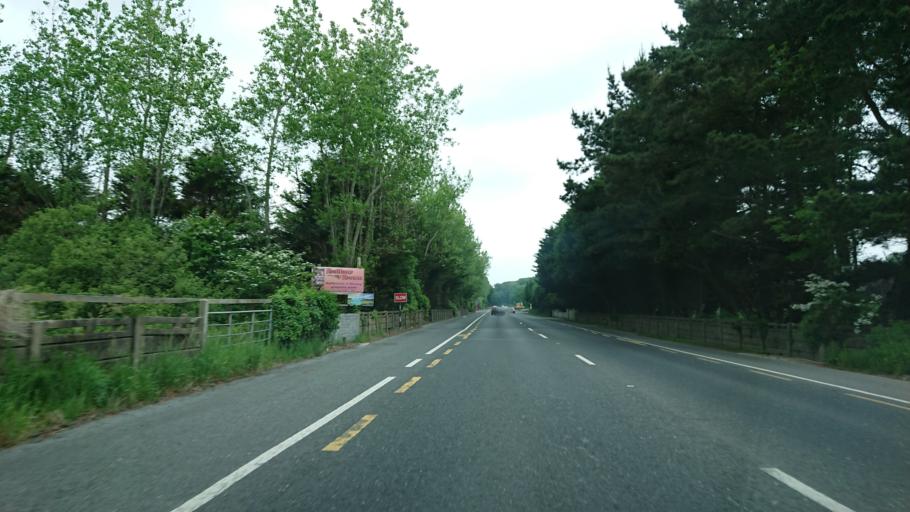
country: IE
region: Munster
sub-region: Waterford
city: Waterford
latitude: 52.2044
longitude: -7.1162
